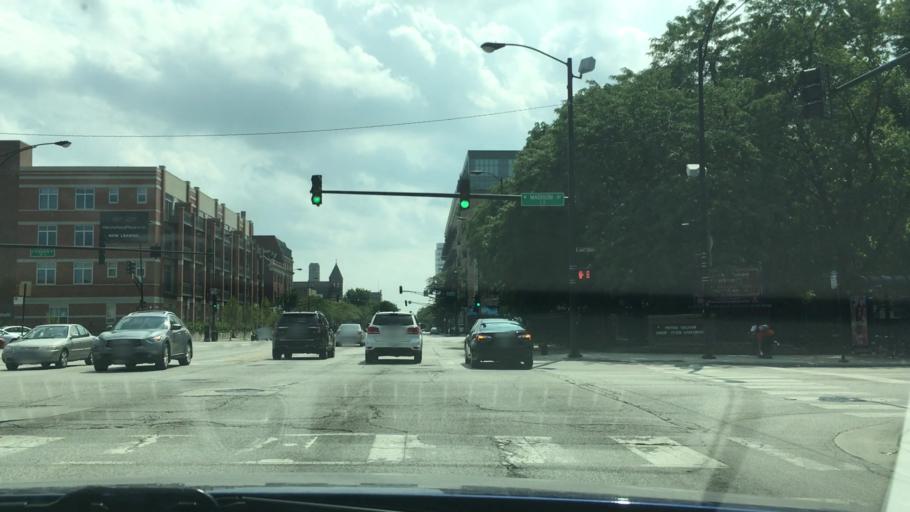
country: US
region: Illinois
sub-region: Cook County
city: Chicago
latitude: 41.8816
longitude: -87.6669
